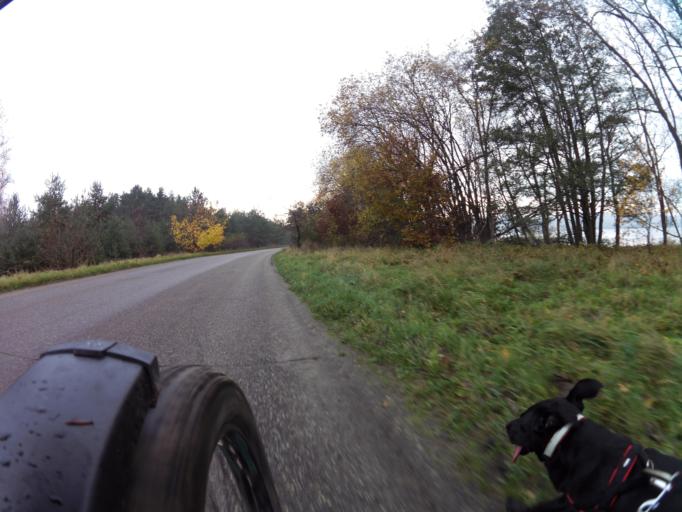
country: PL
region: Pomeranian Voivodeship
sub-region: Powiat wejherowski
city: Gniewino
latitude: 54.7349
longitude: 18.0926
